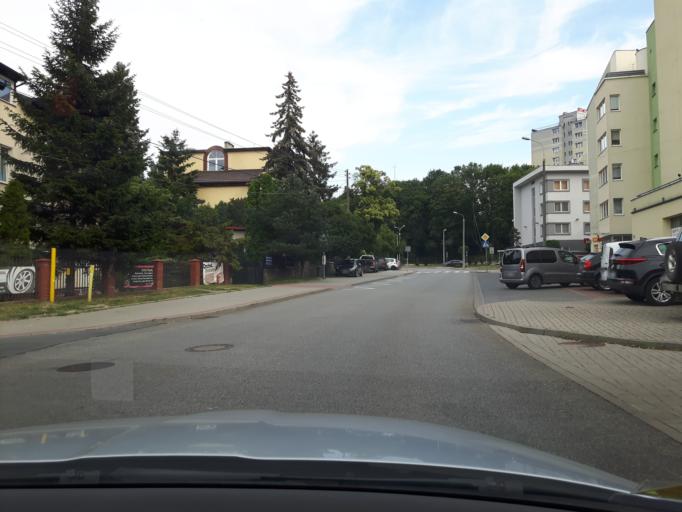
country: PL
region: Pomeranian Voivodeship
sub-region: Gdynia
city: Gdynia
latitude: 54.4971
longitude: 18.5430
